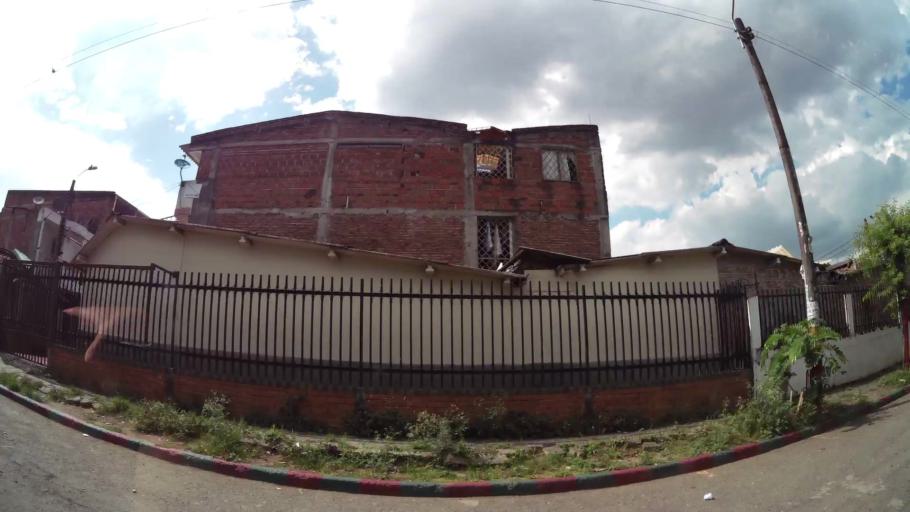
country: CO
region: Valle del Cauca
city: Cali
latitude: 3.3991
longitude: -76.5113
